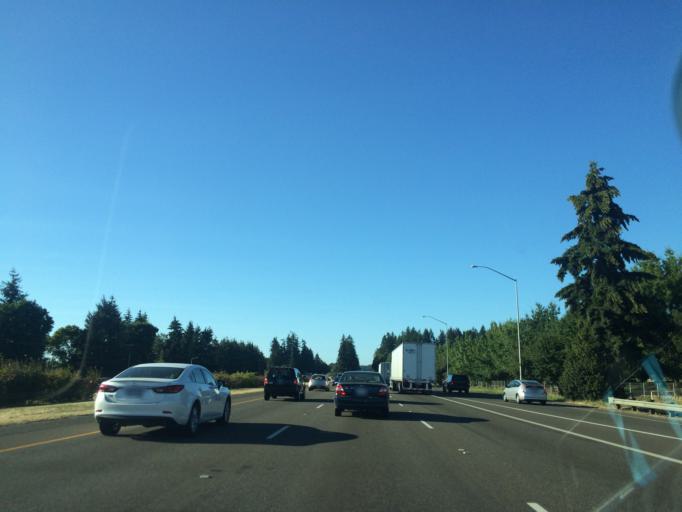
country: US
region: Oregon
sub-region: Clackamas County
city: Wilsonville
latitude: 45.3060
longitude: -122.7691
